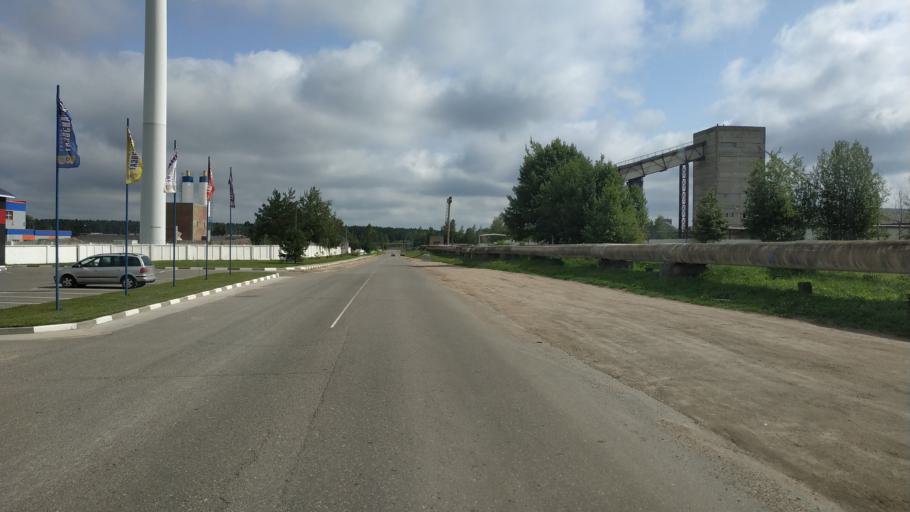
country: BY
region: Mogilev
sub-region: Mahilyowski Rayon
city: Veyno
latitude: 53.8407
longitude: 30.3780
